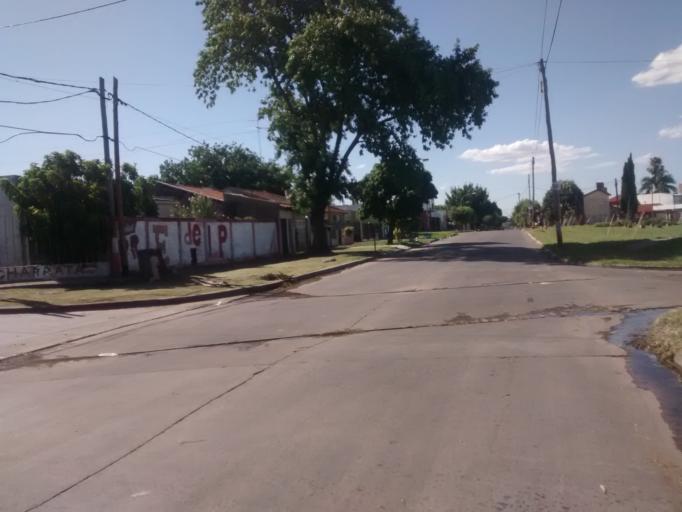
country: AR
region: Buenos Aires
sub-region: Partido de La Plata
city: La Plata
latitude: -34.9307
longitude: -57.9059
